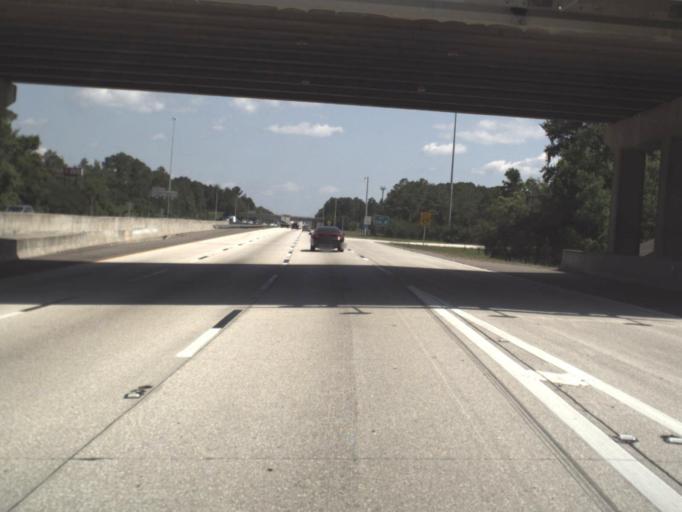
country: US
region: Florida
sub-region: Duval County
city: Jacksonville
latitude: 30.4083
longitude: -81.6573
